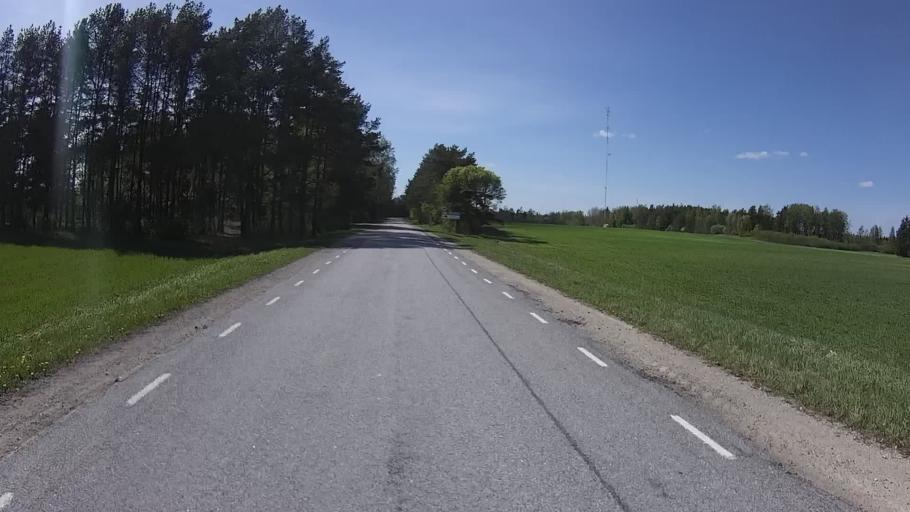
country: EE
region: Laeaene
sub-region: Ridala Parish
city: Uuemoisa
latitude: 59.0012
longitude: 23.7356
